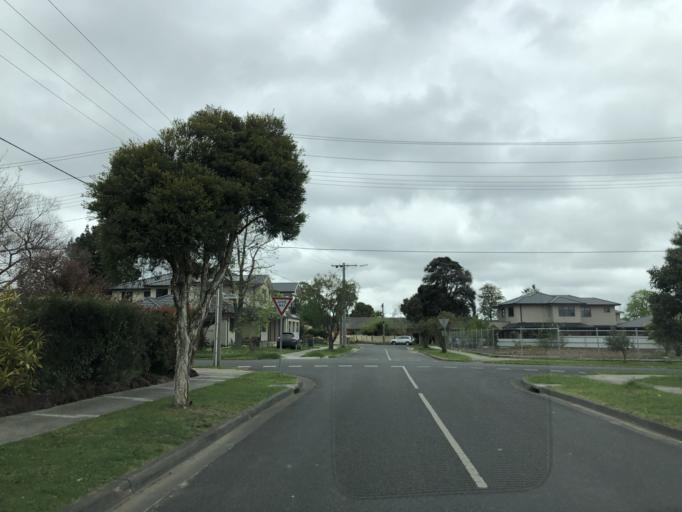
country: AU
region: Victoria
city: Burwood East
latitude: -37.8620
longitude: 145.1491
